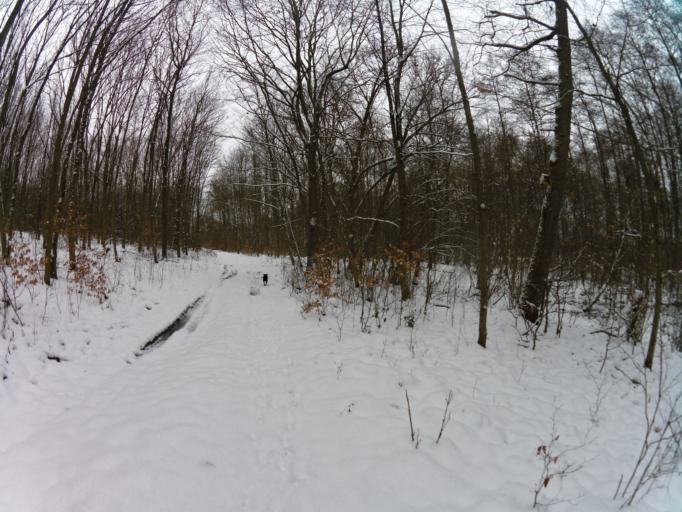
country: PL
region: West Pomeranian Voivodeship
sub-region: Powiat choszczenski
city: Recz
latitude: 53.3304
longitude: 15.5462
